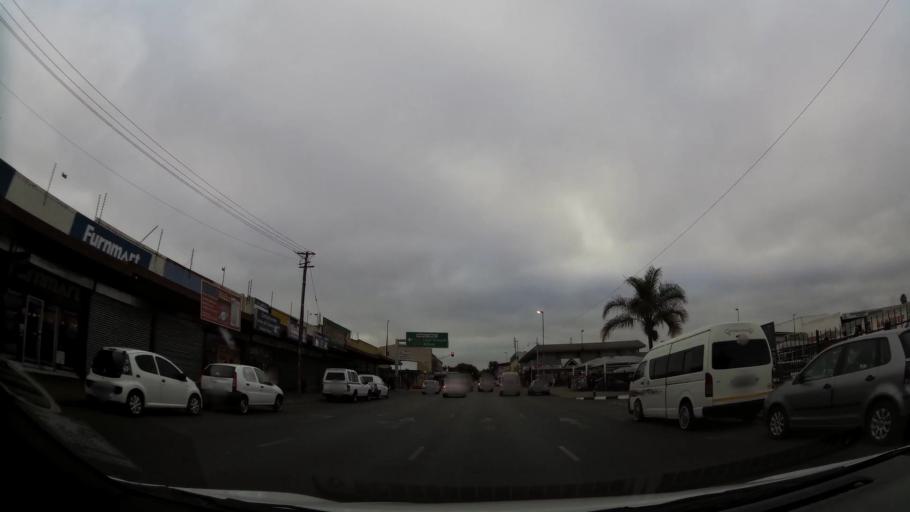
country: ZA
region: Limpopo
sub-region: Capricorn District Municipality
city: Polokwane
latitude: -23.9028
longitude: 29.4494
